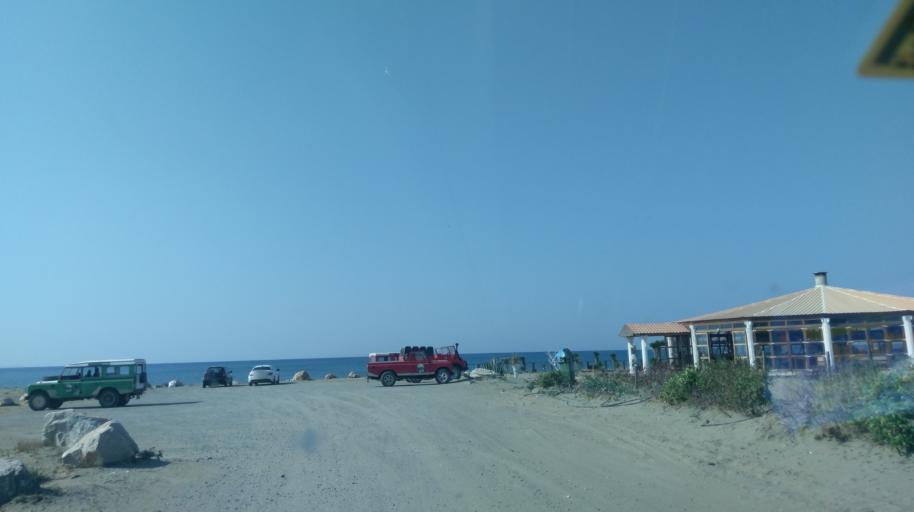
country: CY
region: Lefkosia
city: Morfou
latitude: 35.2816
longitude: 32.9390
